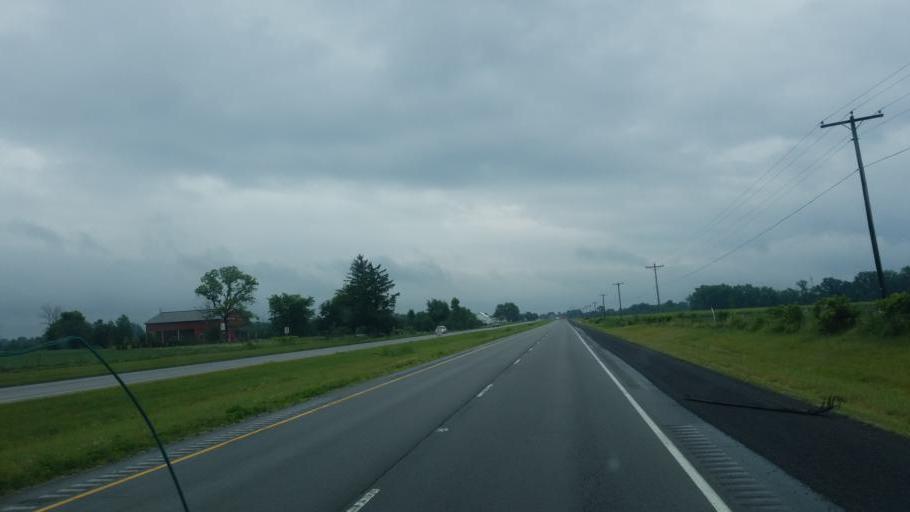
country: US
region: Indiana
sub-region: Wells County
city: Ossian
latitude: 40.9562
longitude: -85.0686
